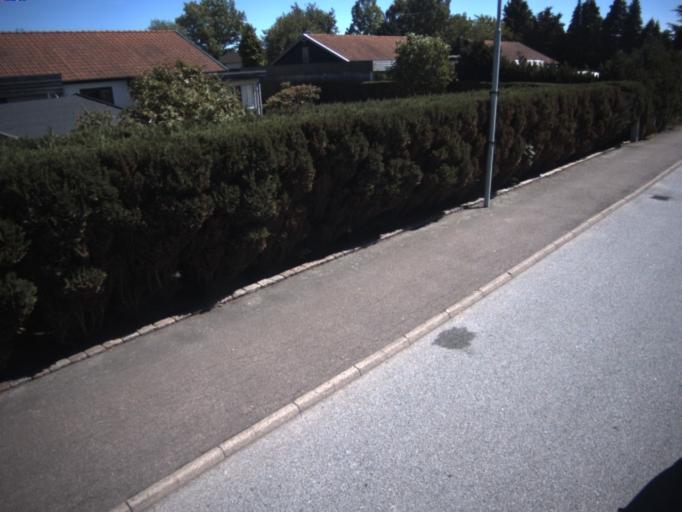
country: SE
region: Skane
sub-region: Helsingborg
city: Morarp
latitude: 56.0637
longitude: 12.8771
